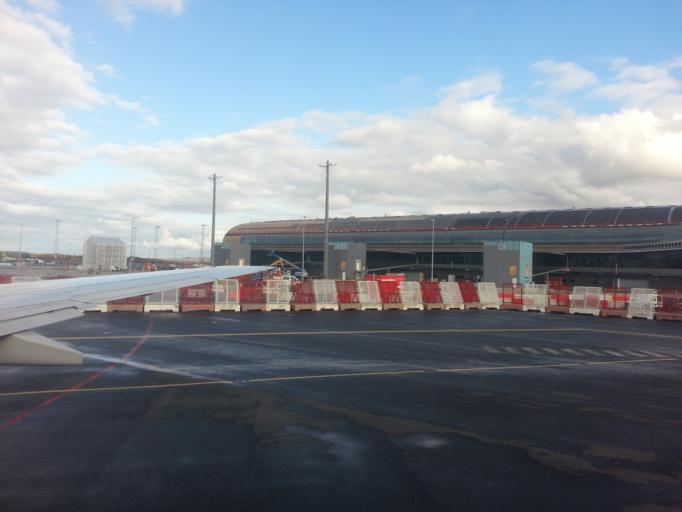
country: NO
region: Akershus
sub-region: Nannestad
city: Teigebyen
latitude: 60.1960
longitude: 11.0973
